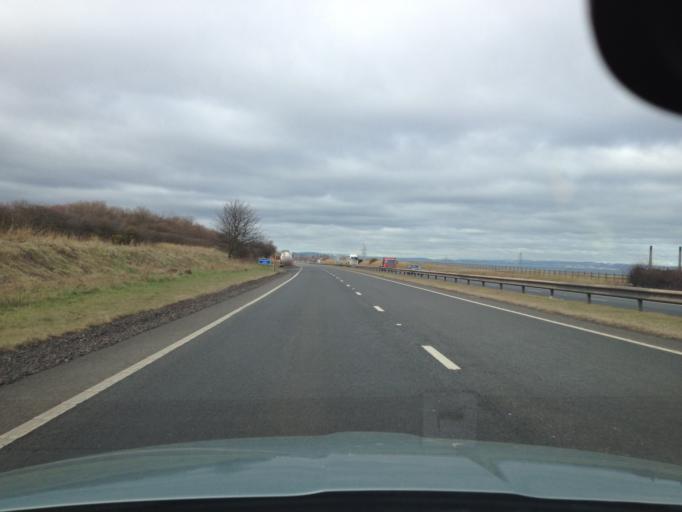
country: GB
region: Scotland
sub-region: East Lothian
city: Tranent
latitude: 55.9520
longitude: -2.9359
